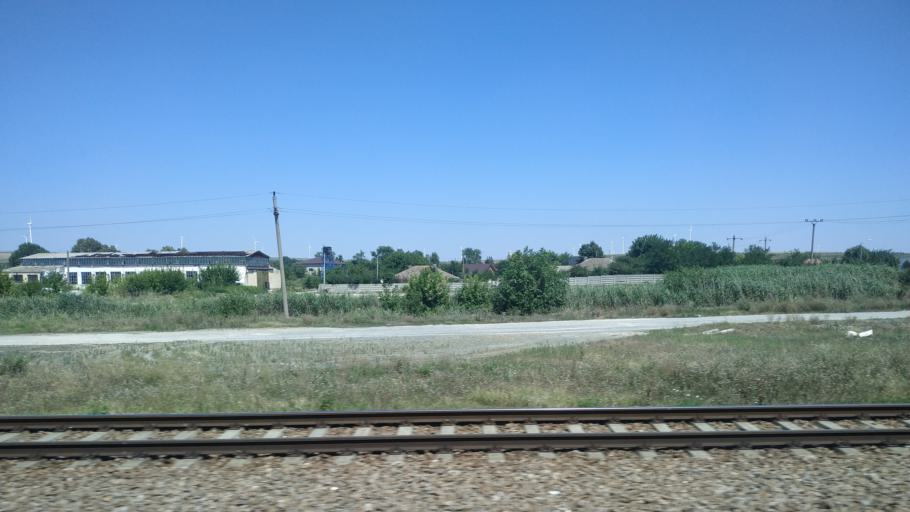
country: RO
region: Constanta
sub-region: Comuna Mircea Voda
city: Mircea Voda
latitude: 44.2668
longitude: 28.1397
